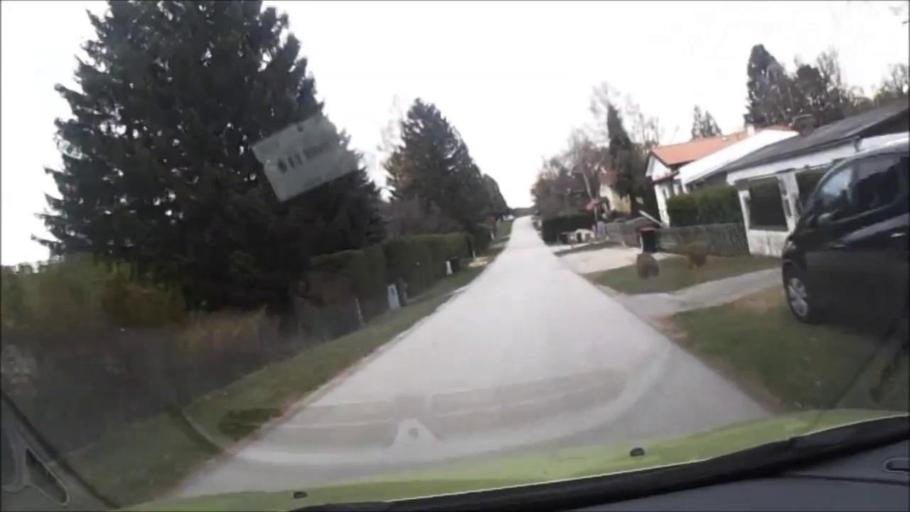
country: AT
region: Burgenland
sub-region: Eisenstadt-Umgebung
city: Loretto
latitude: 47.9005
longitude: 16.5205
